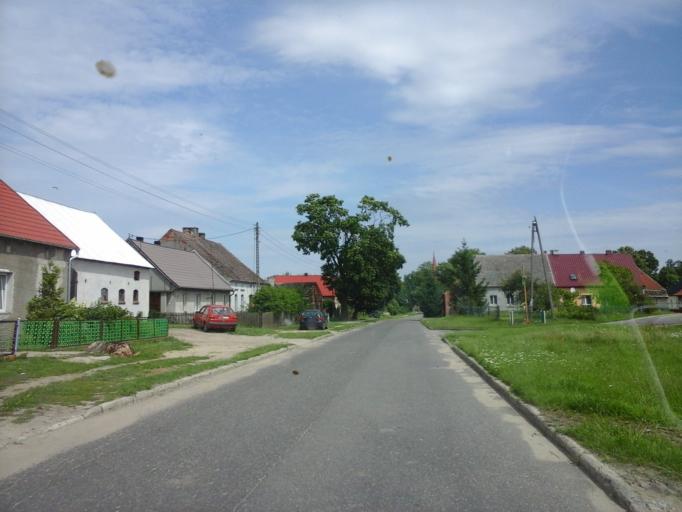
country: PL
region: Lubusz
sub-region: Powiat strzelecko-drezdenecki
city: Dobiegniew
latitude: 53.0127
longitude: 15.7369
